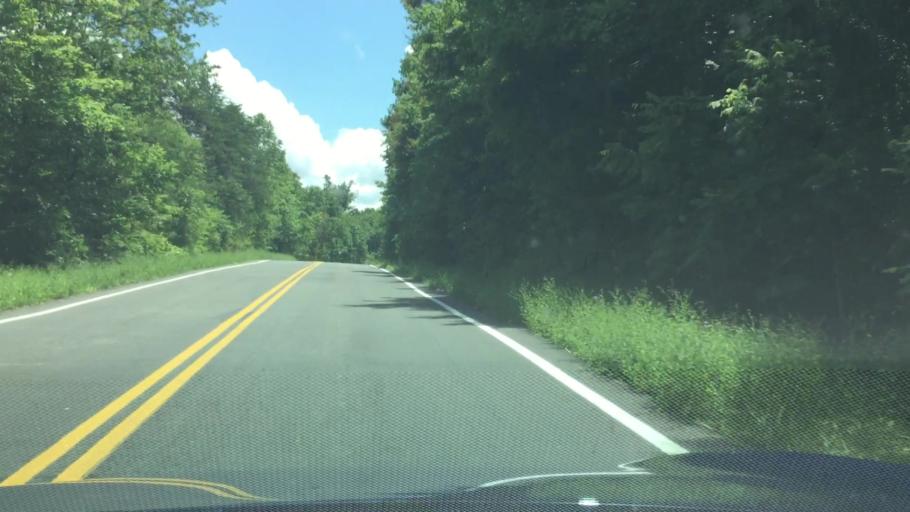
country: US
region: Virginia
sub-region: Pulaski County
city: Pulaski
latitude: 37.0277
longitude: -80.7317
